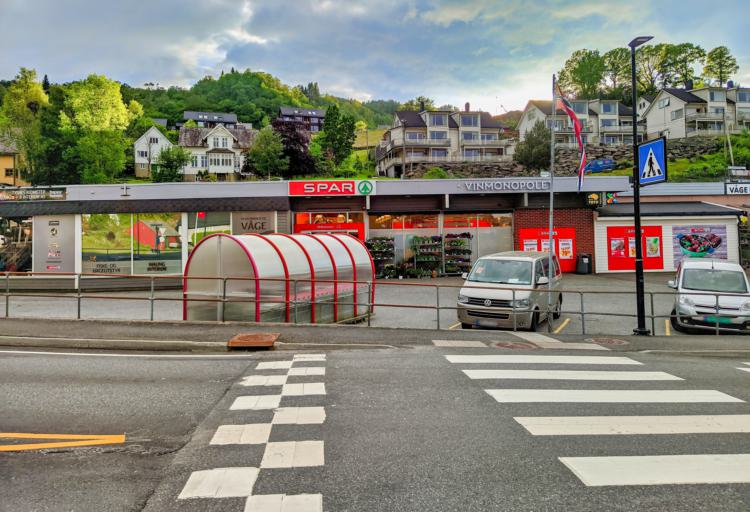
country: NO
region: Hordaland
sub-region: Tysnes
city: Uggdal
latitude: 60.0437
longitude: 5.5228
